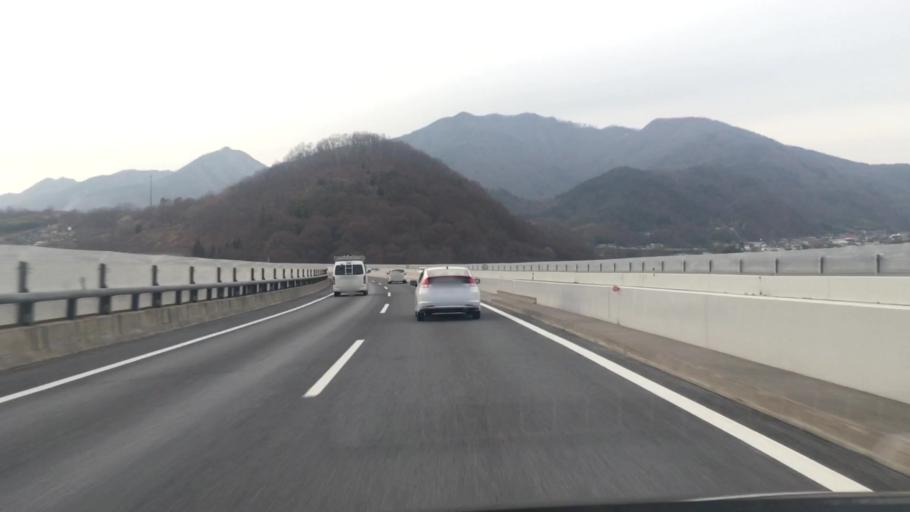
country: JP
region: Nagano
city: Ueda
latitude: 36.4077
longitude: 138.3076
